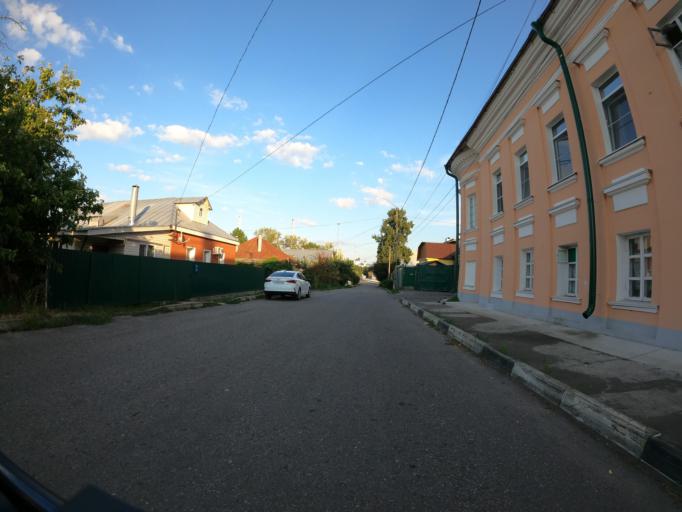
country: RU
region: Moskovskaya
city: Raduzhnyy
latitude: 55.1084
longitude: 38.7503
